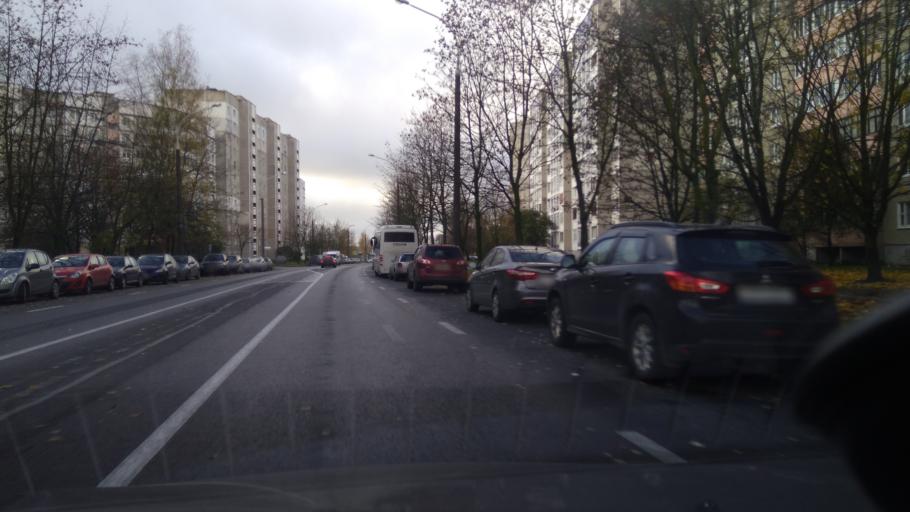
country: BY
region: Minsk
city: Malinovka
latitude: 53.8583
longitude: 27.4354
